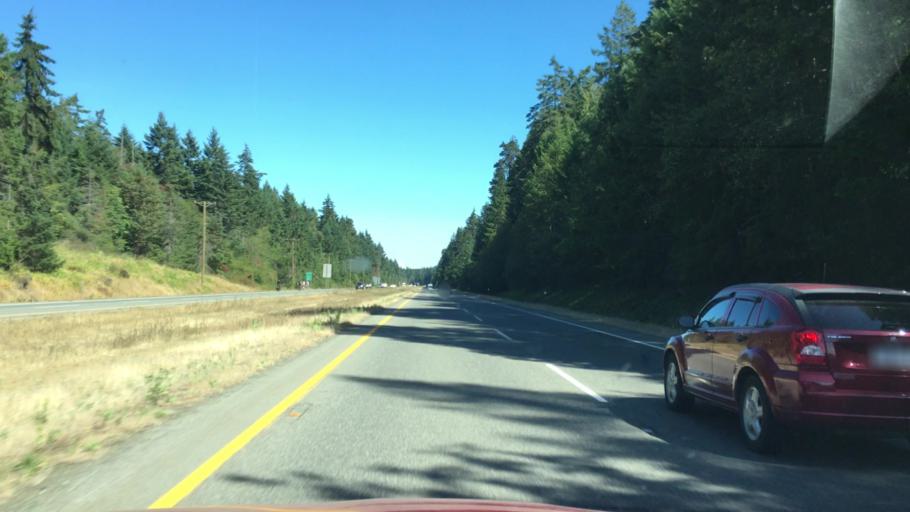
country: CA
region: British Columbia
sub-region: Regional District of Nanaimo
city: Parksville
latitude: 49.3023
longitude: -124.3039
